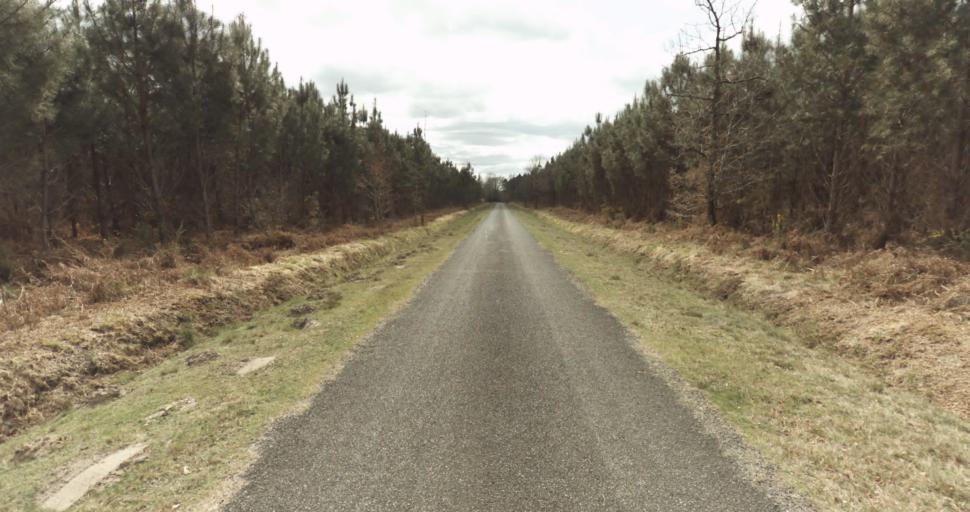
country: FR
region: Aquitaine
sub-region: Departement des Landes
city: Roquefort
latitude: 44.0838
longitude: -0.3881
